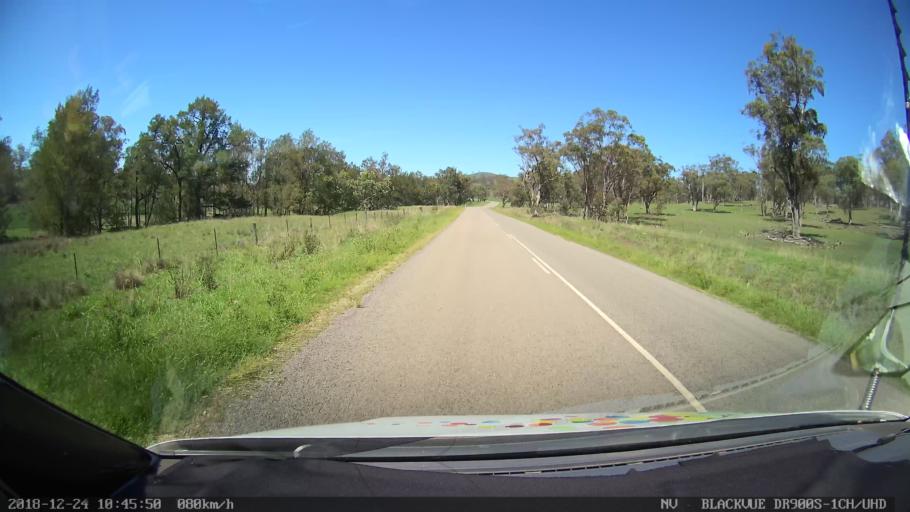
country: AU
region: New South Wales
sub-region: Upper Hunter Shire
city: Merriwa
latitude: -31.9065
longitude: 150.4329
